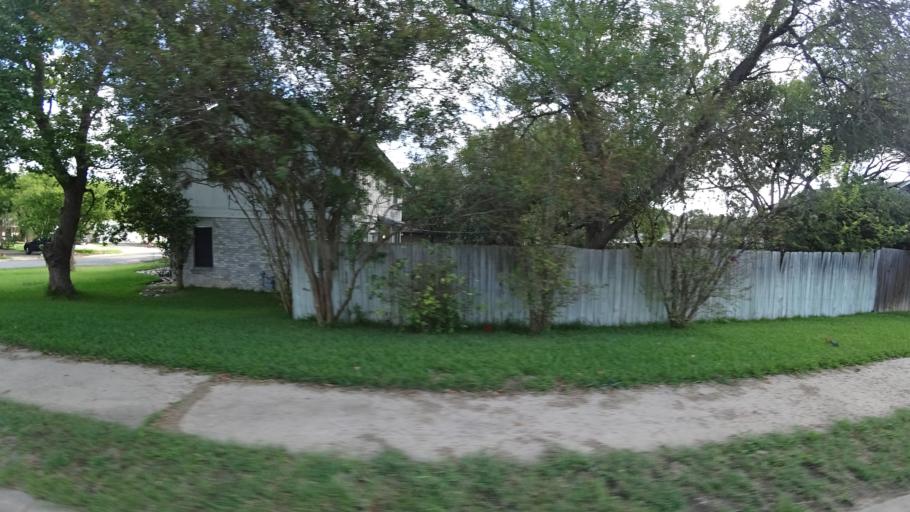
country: US
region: Texas
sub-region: Travis County
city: Shady Hollow
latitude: 30.2127
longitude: -97.8148
